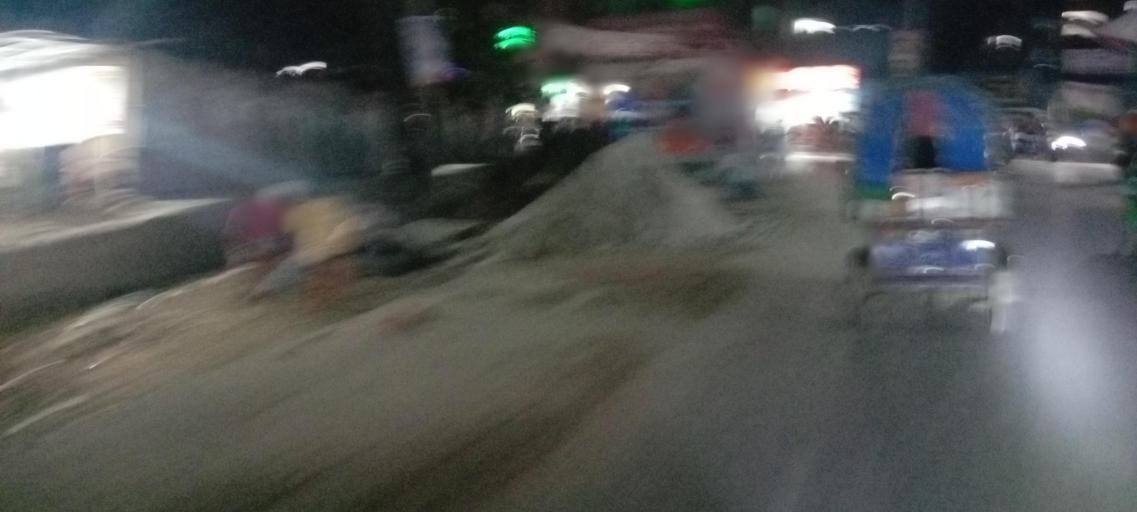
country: BD
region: Dhaka
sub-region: Dhaka
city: Dhaka
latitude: 23.7028
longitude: 90.3897
